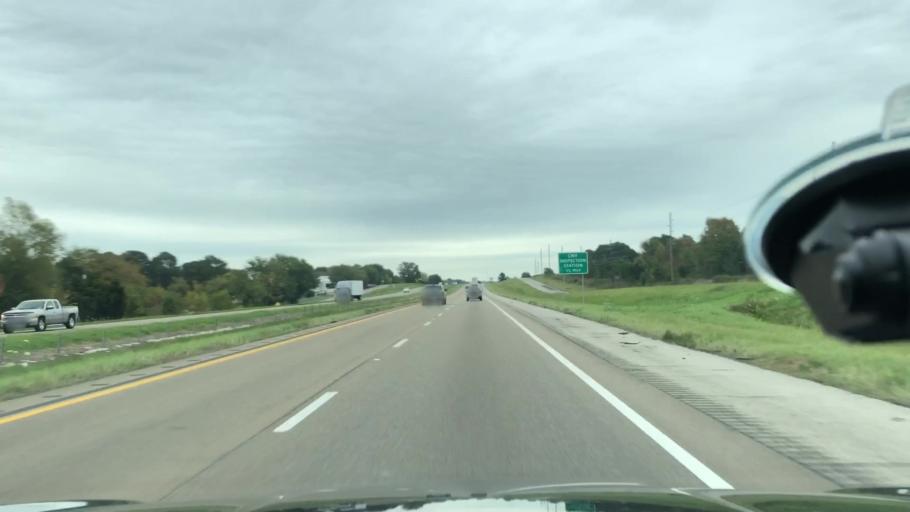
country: US
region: Texas
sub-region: Titus County
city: Mount Pleasant
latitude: 33.1590
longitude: -95.0629
